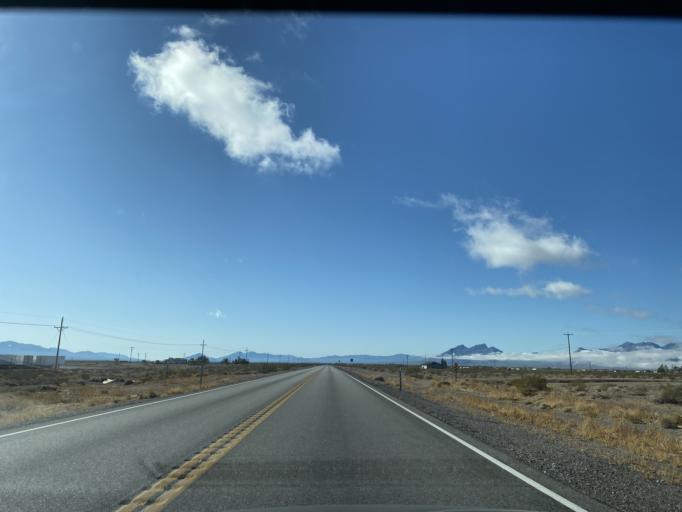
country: US
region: Nevada
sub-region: Nye County
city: Beatty
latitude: 36.5293
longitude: -116.4188
